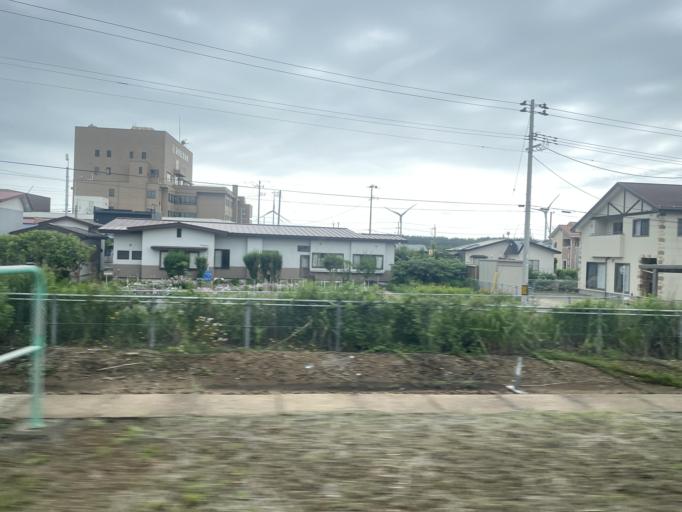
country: JP
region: Akita
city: Tenno
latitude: 39.8808
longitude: 139.9883
